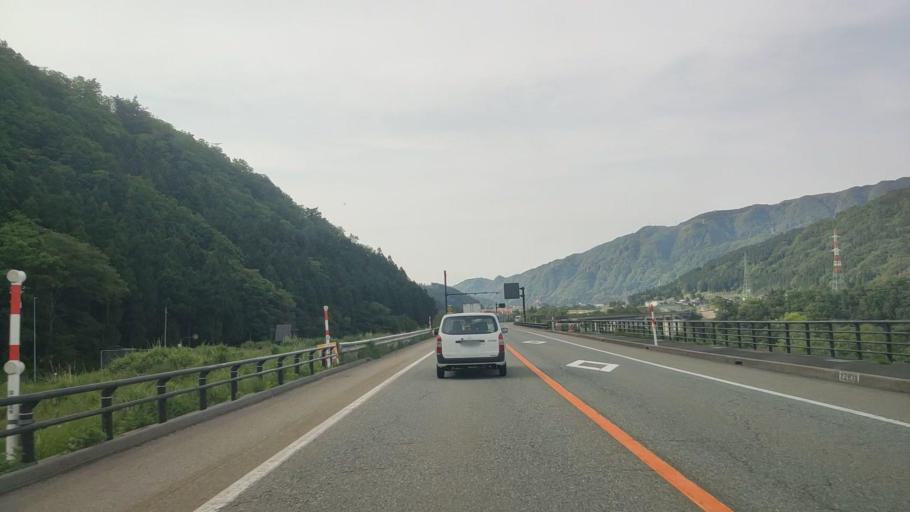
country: JP
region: Toyama
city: Yatsuomachi-higashikumisaka
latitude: 36.5111
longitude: 137.2283
